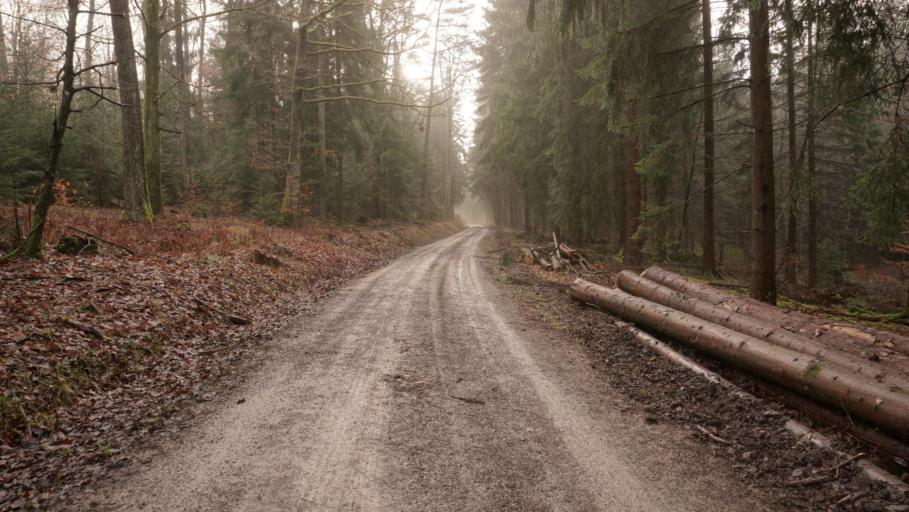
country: DE
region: Baden-Wuerttemberg
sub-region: Karlsruhe Region
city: Reichartshausen
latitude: 49.4103
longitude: 8.9544
